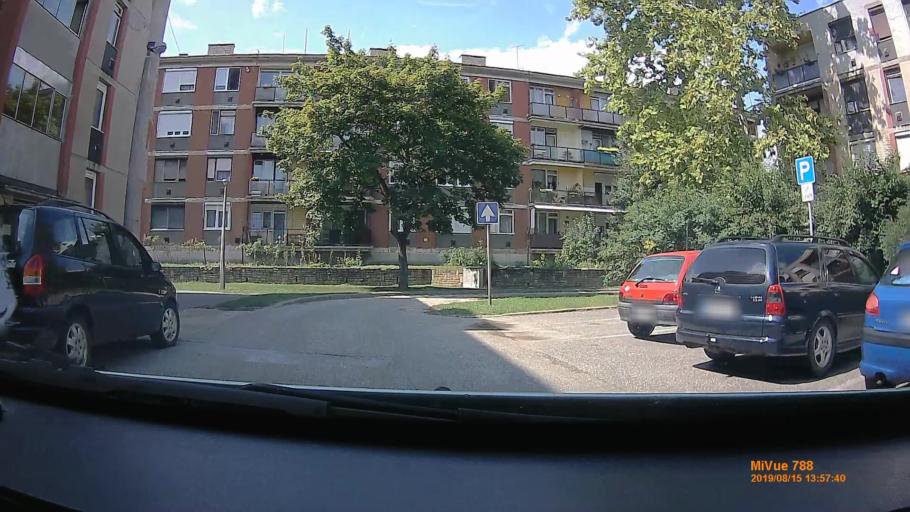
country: HU
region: Borsod-Abauj-Zemplen
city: Kazincbarcika
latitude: 48.2523
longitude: 20.6175
